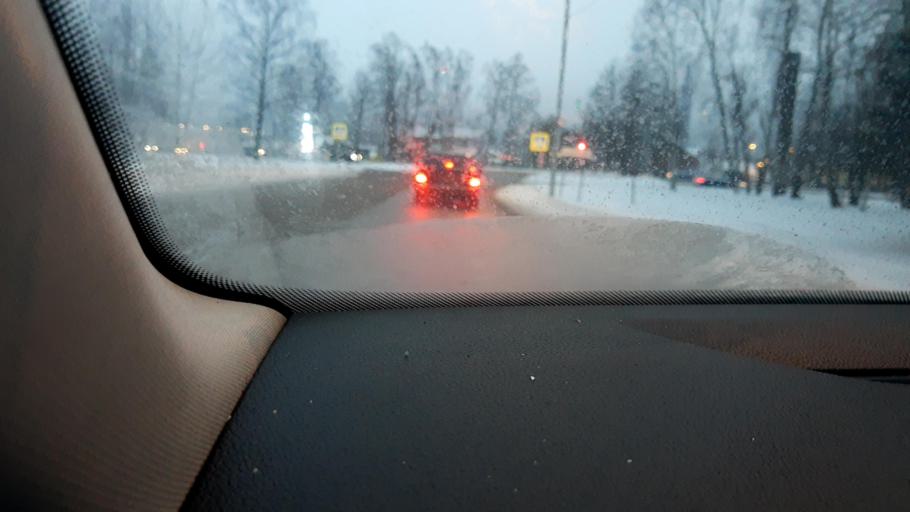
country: RU
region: Moskovskaya
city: Troitsk
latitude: 55.3009
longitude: 37.2025
